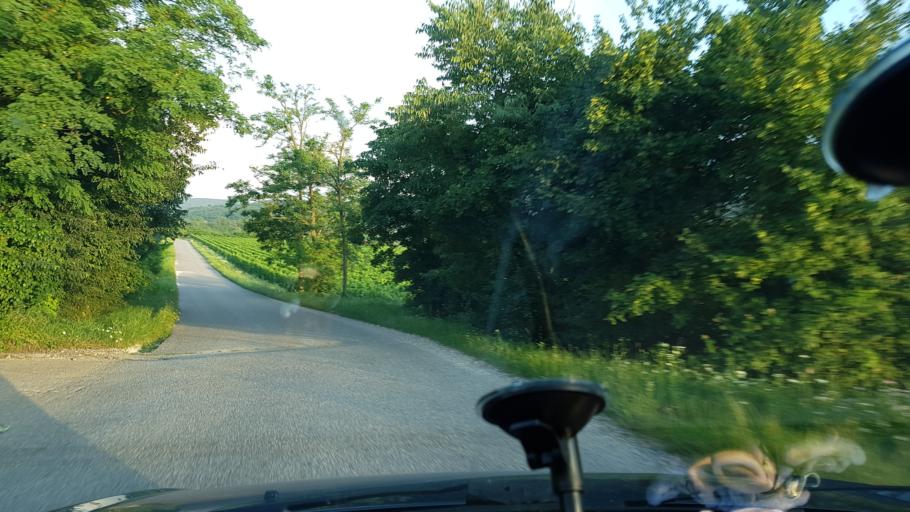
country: IT
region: Friuli Venezia Giulia
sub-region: Provincia di Gorizia
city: Mossa
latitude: 45.9117
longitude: 13.5479
